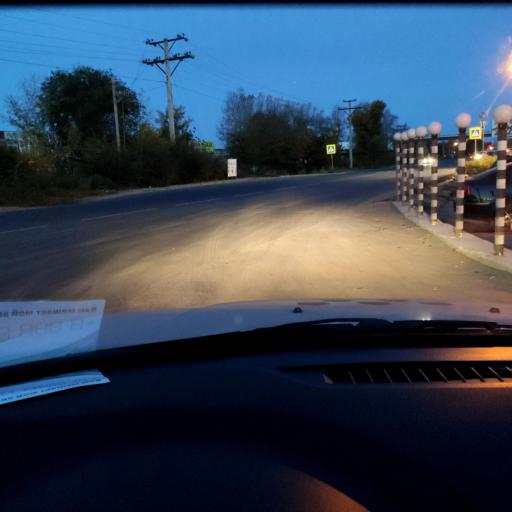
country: RU
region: Samara
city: Tol'yatti
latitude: 53.5338
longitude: 49.4478
